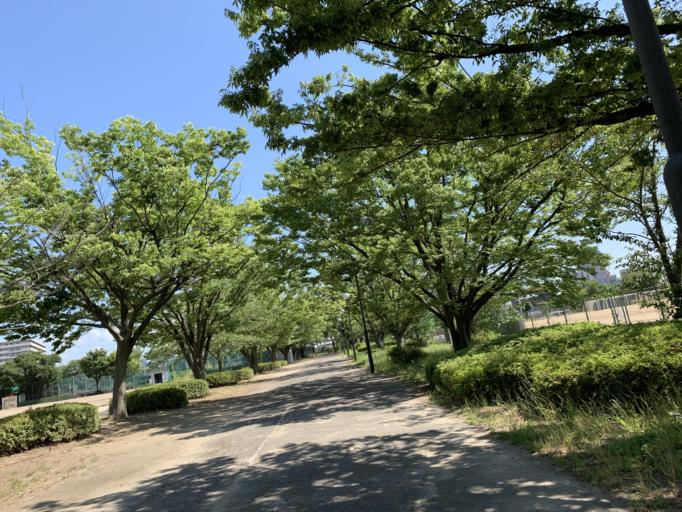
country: JP
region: Osaka
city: Sakai
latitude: 34.5890
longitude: 135.5043
